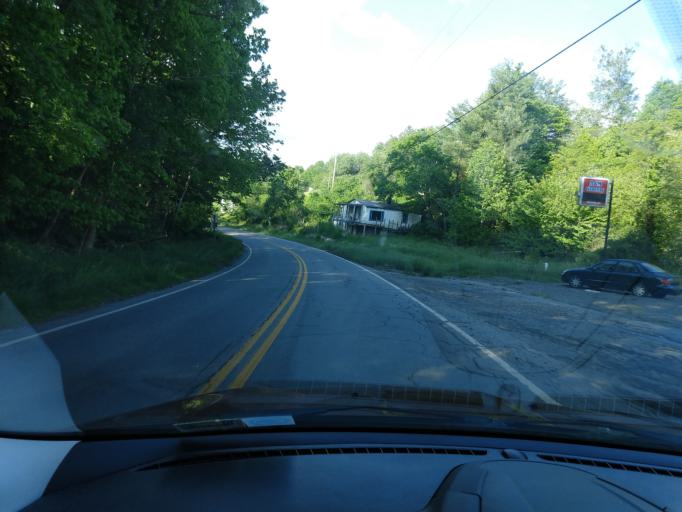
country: US
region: Virginia
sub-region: City of Galax
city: Galax
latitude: 36.7492
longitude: -80.9864
